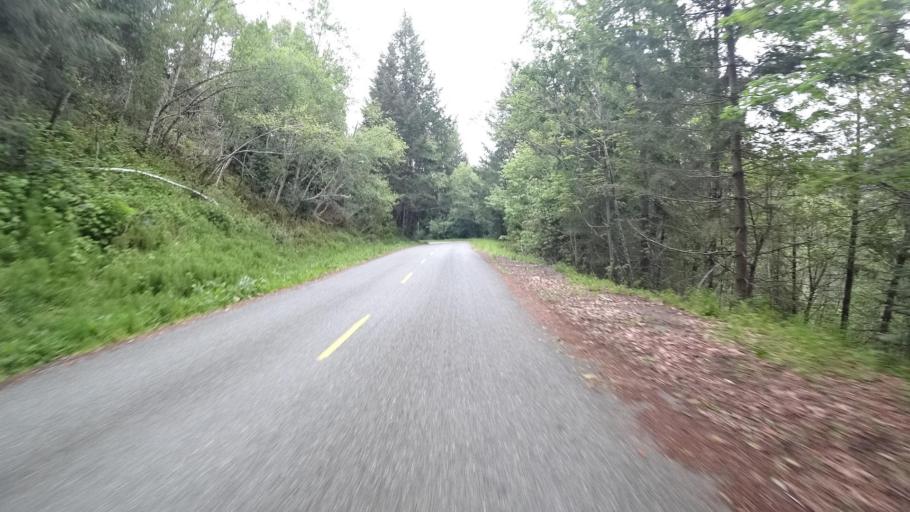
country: US
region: California
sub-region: Humboldt County
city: Blue Lake
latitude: 40.9443
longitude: -123.8425
